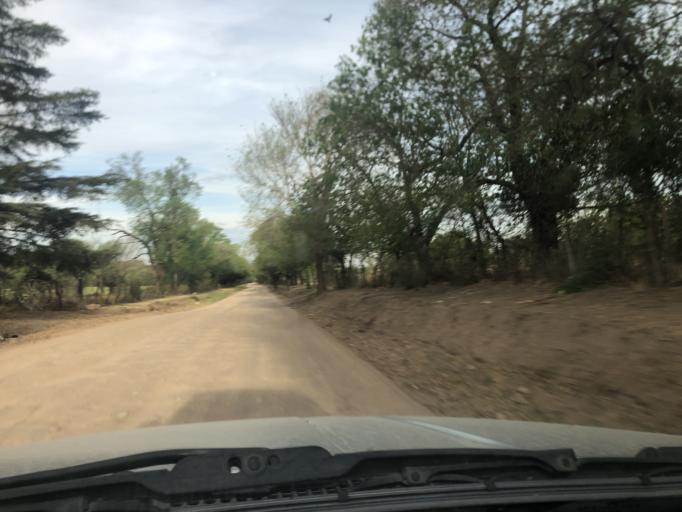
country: AR
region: Cordoba
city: La Granja
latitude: -31.0176
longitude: -64.2465
